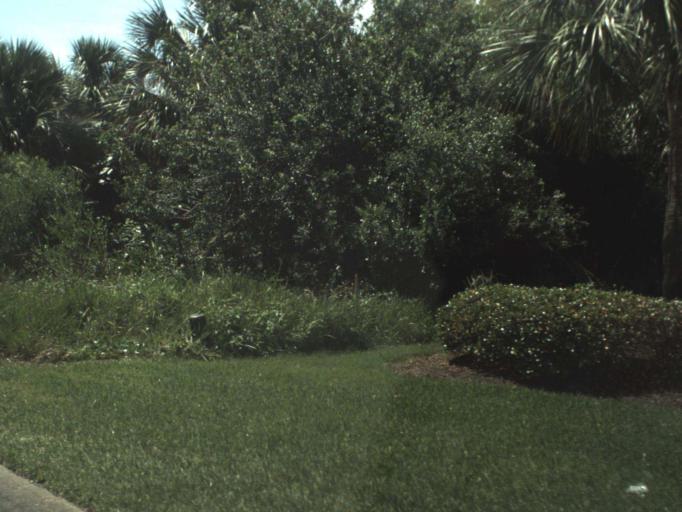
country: US
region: Florida
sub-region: Volusia County
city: Daytona Beach Shores
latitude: 29.1683
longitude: -80.9823
